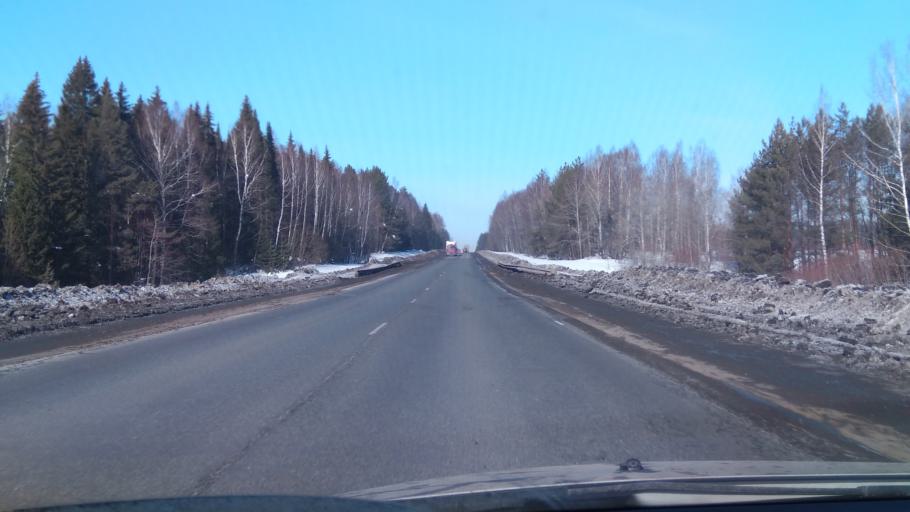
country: RU
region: Perm
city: Kungur
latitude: 57.4353
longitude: 56.8238
